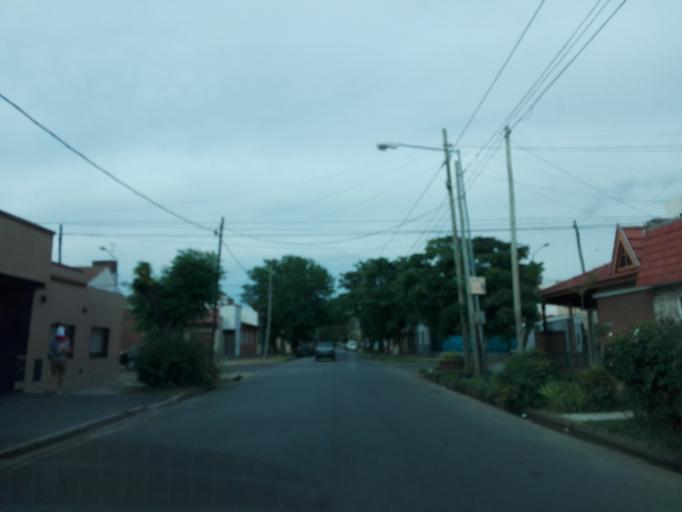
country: AR
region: Buenos Aires
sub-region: Partido de Lanus
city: Lanus
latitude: -34.7180
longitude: -58.3807
